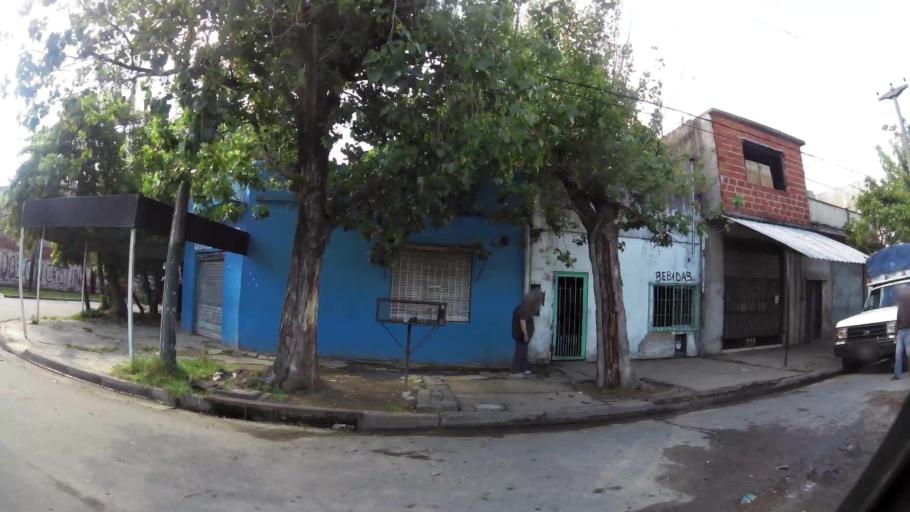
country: AR
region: Buenos Aires F.D.
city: Villa Lugano
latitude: -34.6748
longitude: -58.4320
